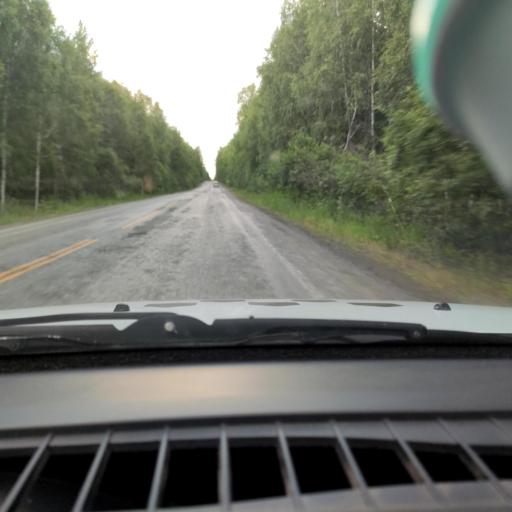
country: RU
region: Chelyabinsk
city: Karabash
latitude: 55.5331
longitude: 60.3434
